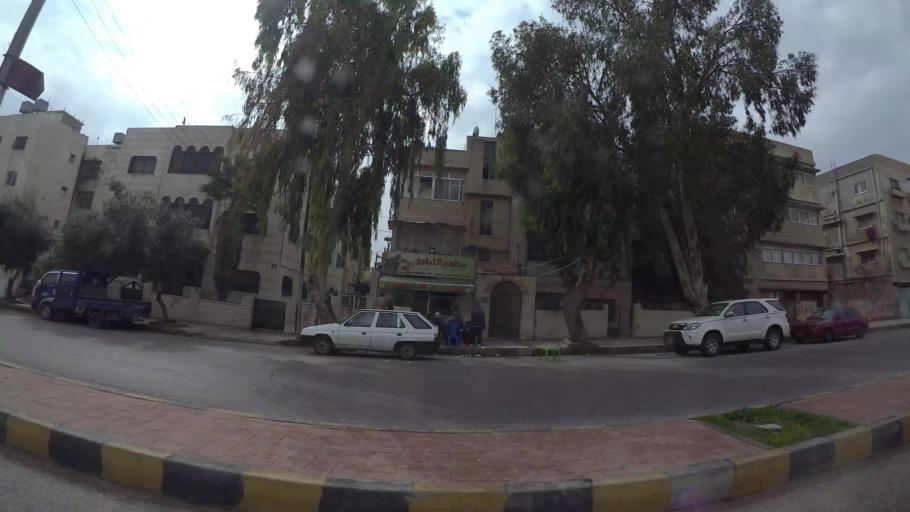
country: JO
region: Amman
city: Amman
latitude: 31.9717
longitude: 35.9315
